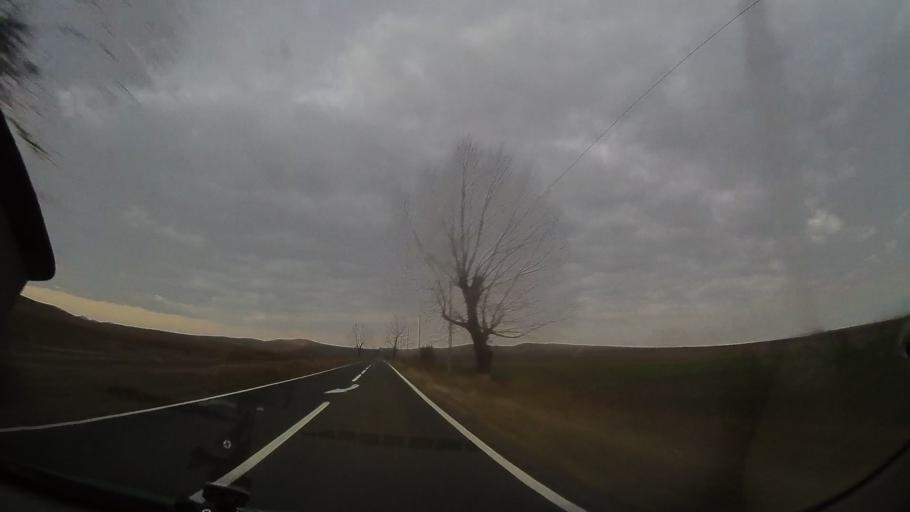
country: RO
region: Tulcea
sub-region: Comuna Nalbant
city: Nicolae Balcescu
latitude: 45.0036
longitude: 28.5971
